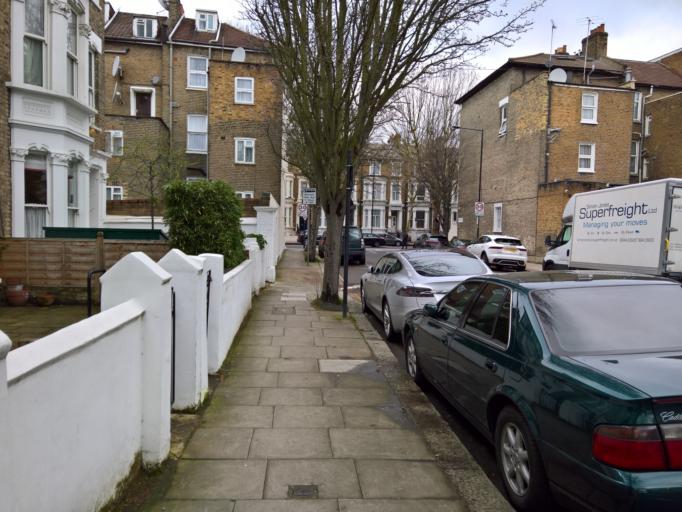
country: GB
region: England
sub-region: Greater London
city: Hammersmith
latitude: 51.4990
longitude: -0.2214
